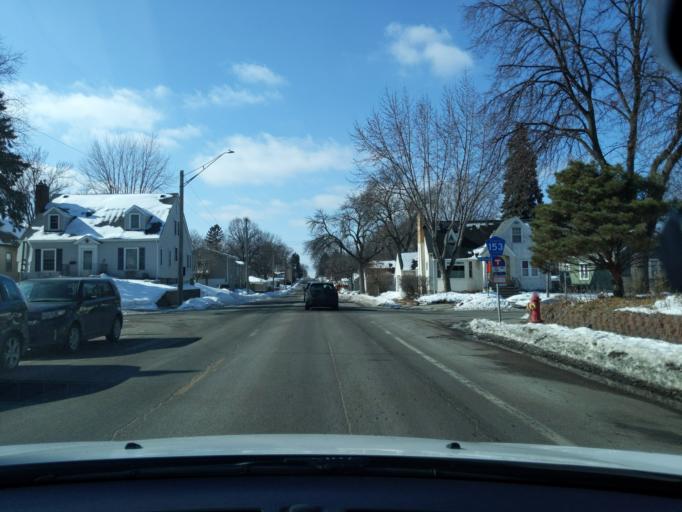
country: US
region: Minnesota
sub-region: Hennepin County
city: Saint Anthony
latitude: 45.0133
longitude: -93.2278
